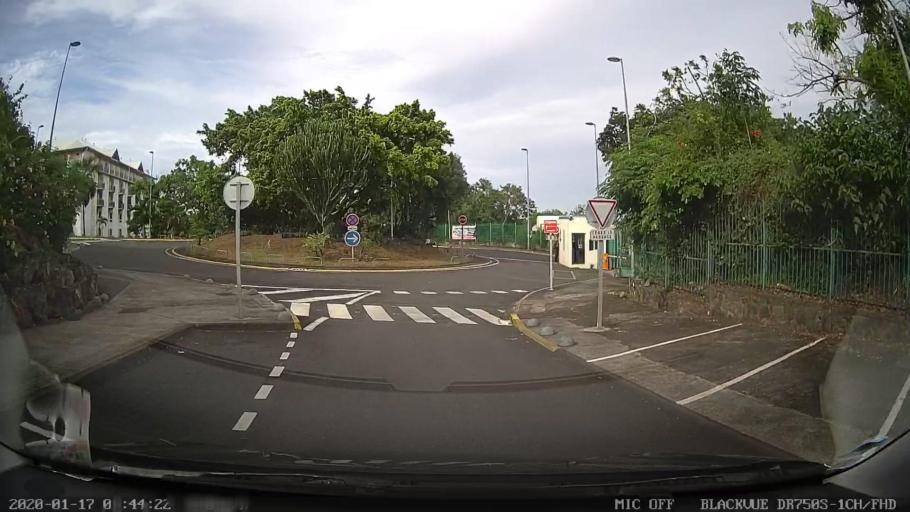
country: RE
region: Reunion
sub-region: Reunion
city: Saint-Denis
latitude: -20.9028
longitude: 55.4863
